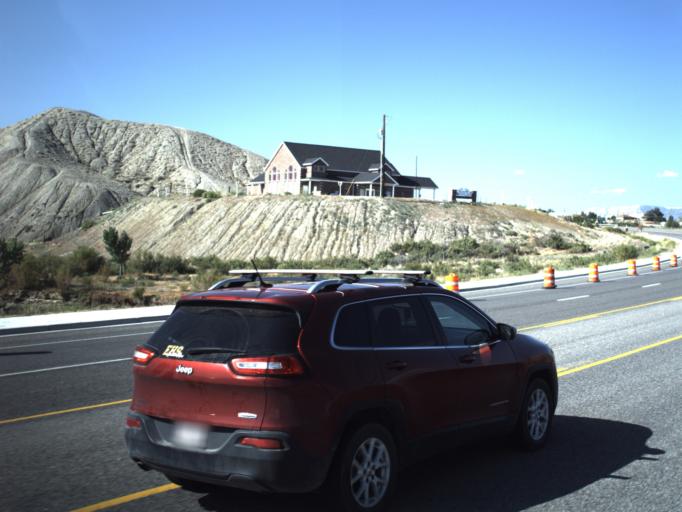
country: US
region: Utah
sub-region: Emery County
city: Huntington
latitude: 39.3390
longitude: -110.9612
